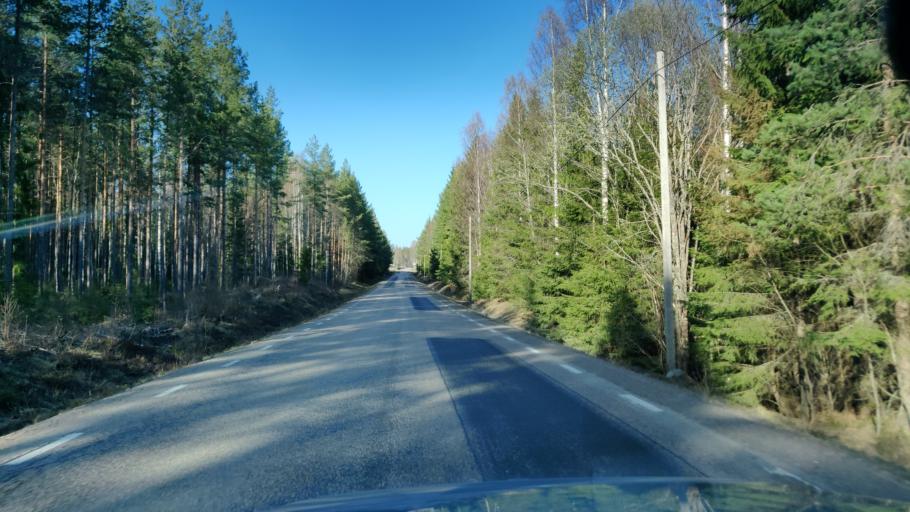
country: SE
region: Vaermland
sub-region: Sunne Kommun
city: Sunne
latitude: 59.9813
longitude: 13.2574
